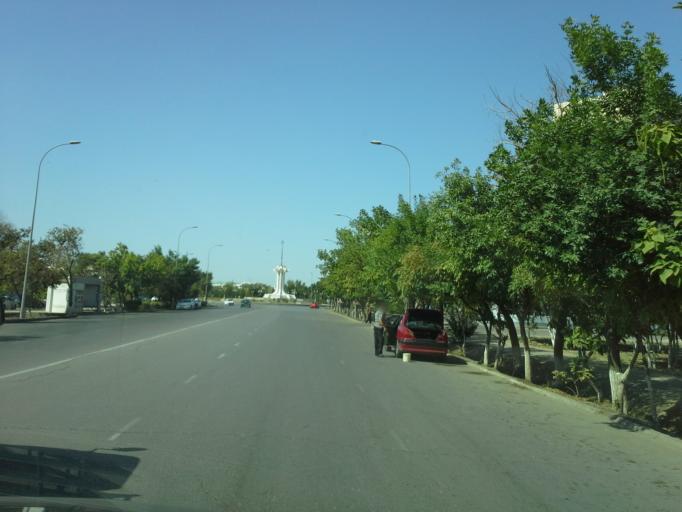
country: TM
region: Dasoguz
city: Dasoguz
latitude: 41.8315
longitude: 59.9719
